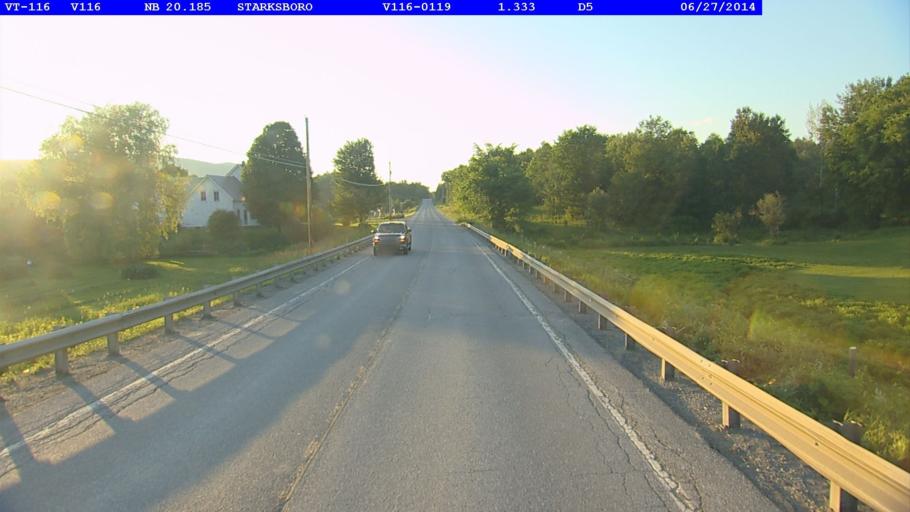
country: US
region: Vermont
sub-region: Addison County
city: Bristol
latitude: 44.2042
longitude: -73.0512
